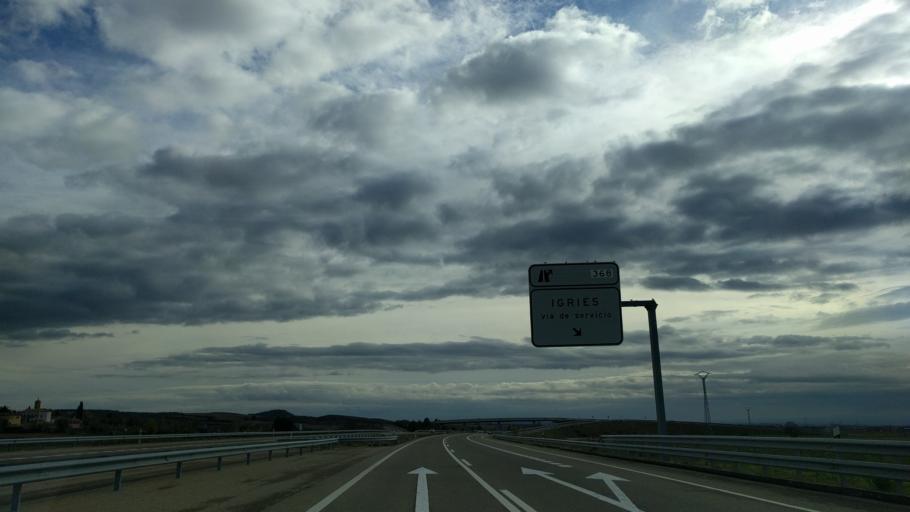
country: ES
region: Aragon
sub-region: Provincia de Huesca
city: Igries
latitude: 42.2160
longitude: -0.4393
